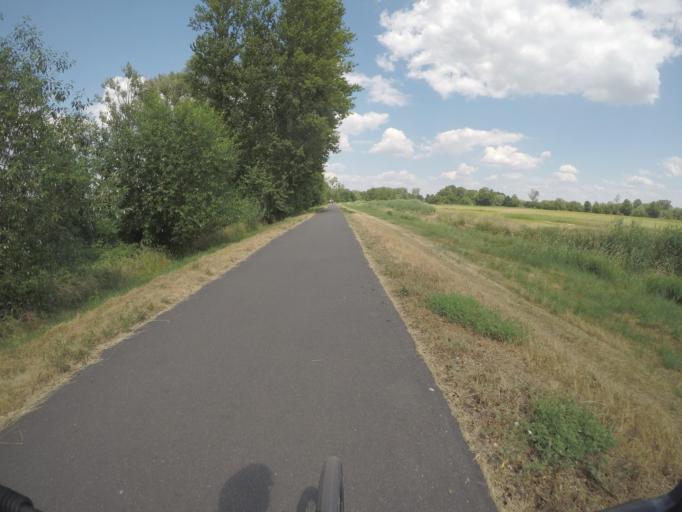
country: DE
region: Brandenburg
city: Roskow
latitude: 52.4310
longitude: 12.6503
